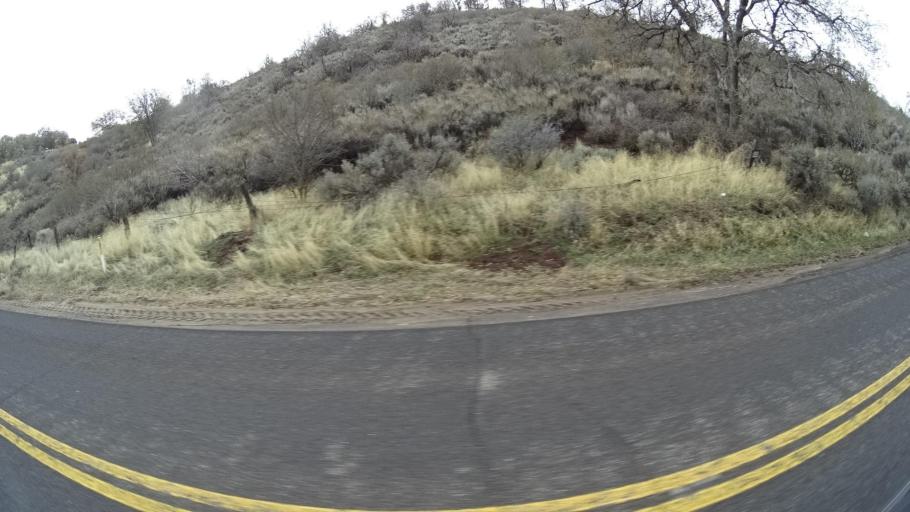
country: US
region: California
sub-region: Kern County
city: Golden Hills
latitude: 35.0953
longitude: -118.5431
